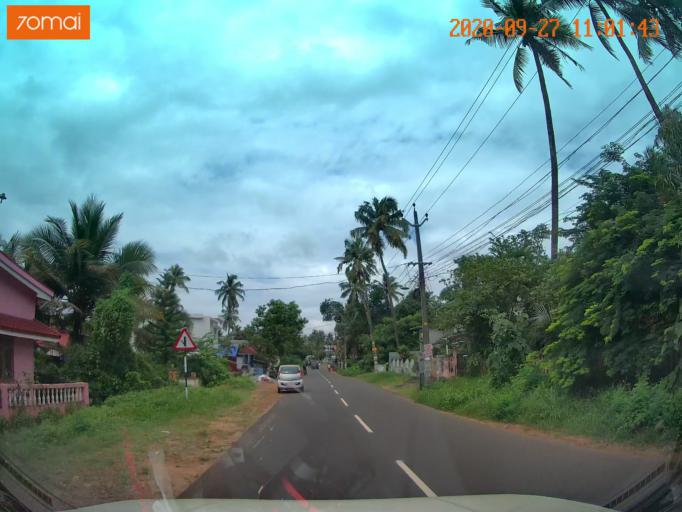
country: IN
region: Kerala
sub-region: Thrissur District
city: Irinjalakuda
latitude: 10.4200
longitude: 76.2654
